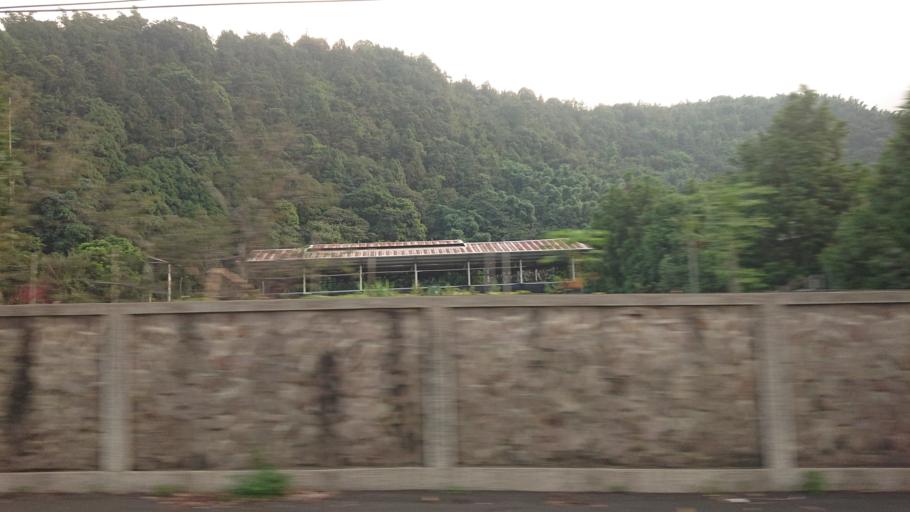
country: TW
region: Taiwan
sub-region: Nantou
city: Puli
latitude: 23.9724
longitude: 120.9953
